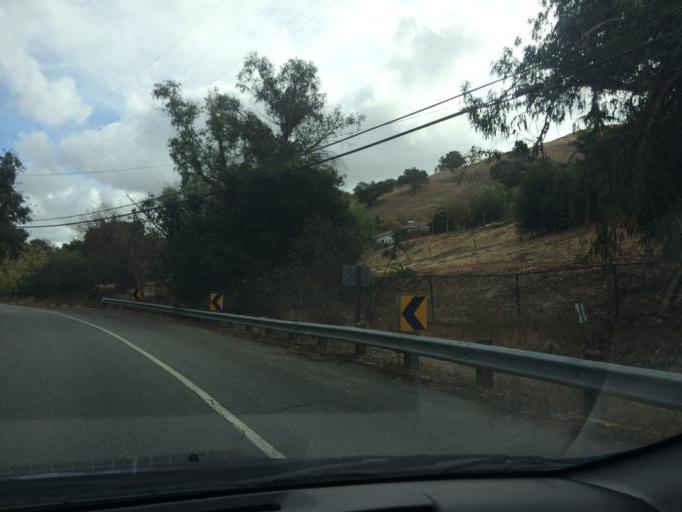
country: US
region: California
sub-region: Santa Clara County
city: Seven Trees
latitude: 37.2737
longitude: -121.7460
